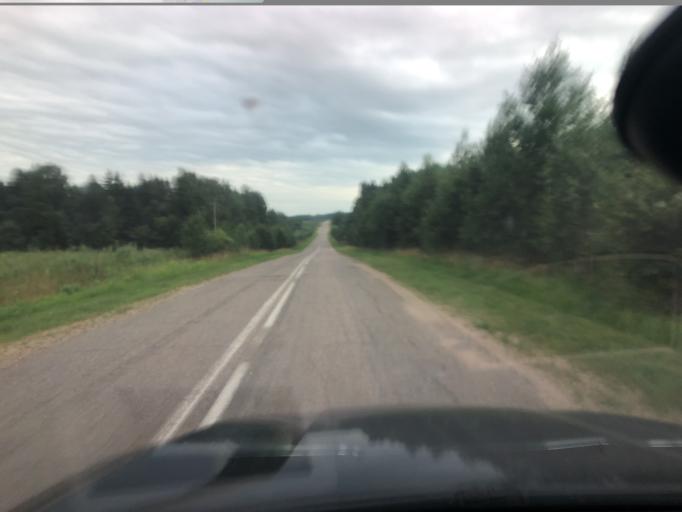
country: RU
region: Jaroslavl
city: Pereslavl'-Zalesskiy
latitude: 57.0254
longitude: 38.9325
